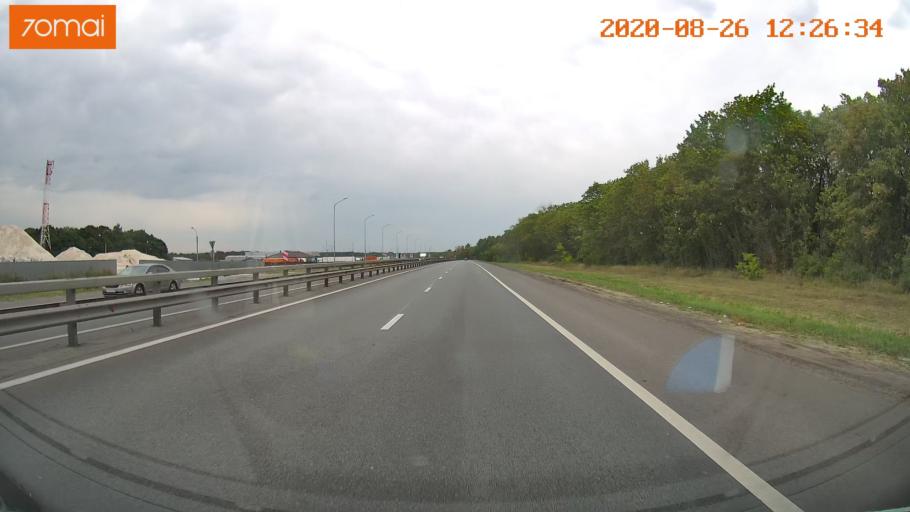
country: RU
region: Rjazan
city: Polyany
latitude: 54.5362
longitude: 39.8575
